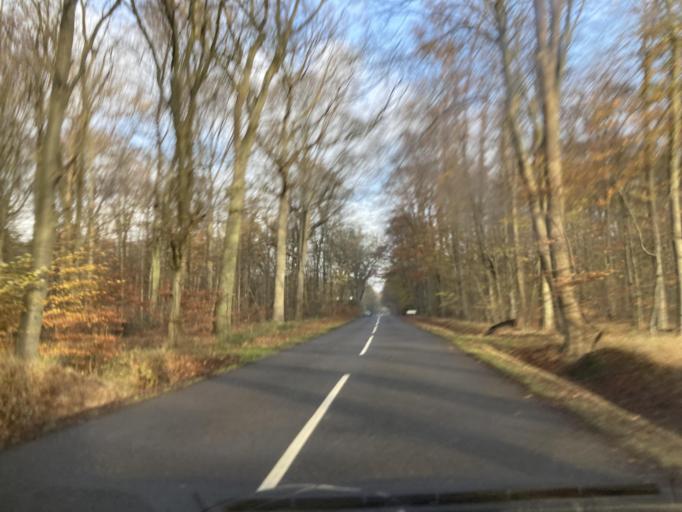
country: DK
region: Zealand
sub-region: Lolland Kommune
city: Rodby
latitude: 54.7738
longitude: 11.3659
